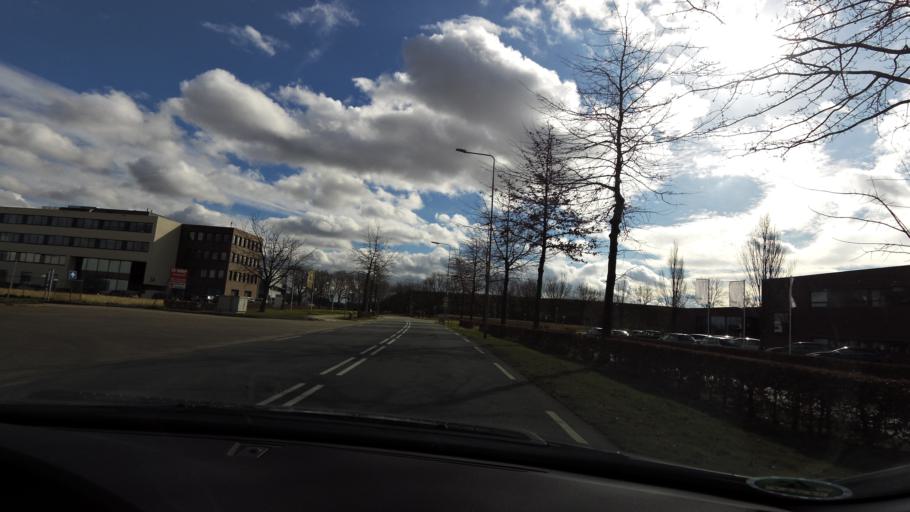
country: NL
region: Limburg
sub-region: Gemeente Beek
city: Beek
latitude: 50.9208
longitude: 5.7887
